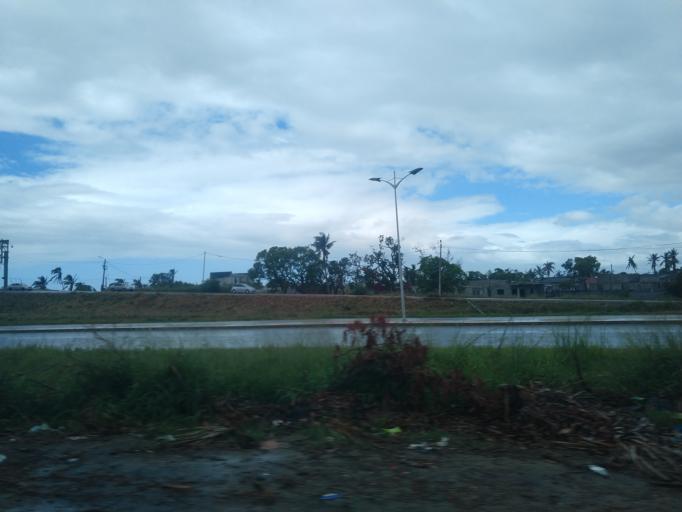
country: MZ
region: Sofala
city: Beira
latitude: -19.7834
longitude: 34.8775
